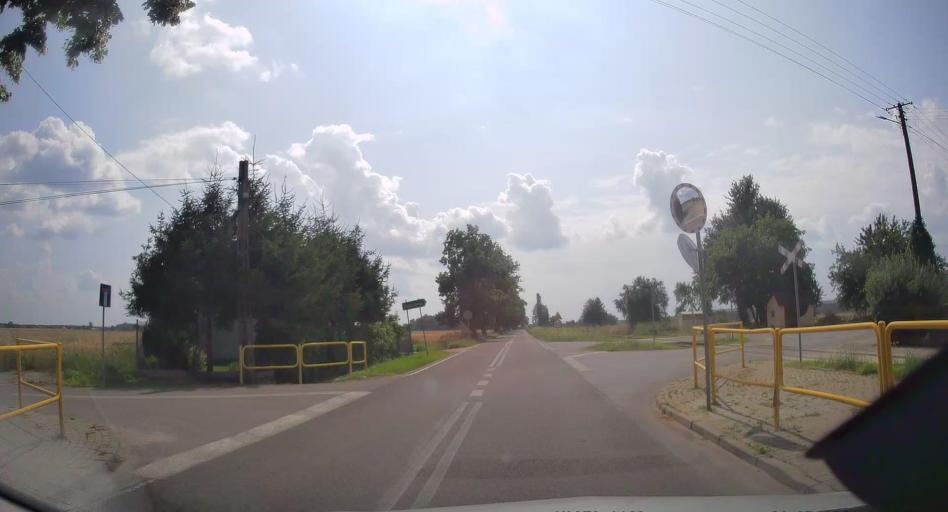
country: PL
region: Lodz Voivodeship
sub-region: Powiat tomaszowski
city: Lubochnia
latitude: 51.5731
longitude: 20.0967
